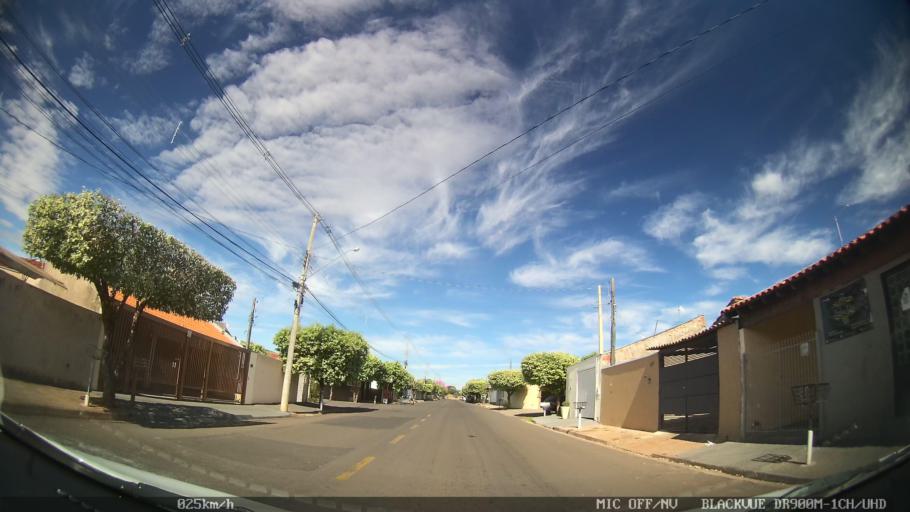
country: BR
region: Sao Paulo
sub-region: Bady Bassitt
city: Bady Bassitt
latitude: -20.8289
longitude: -49.4962
